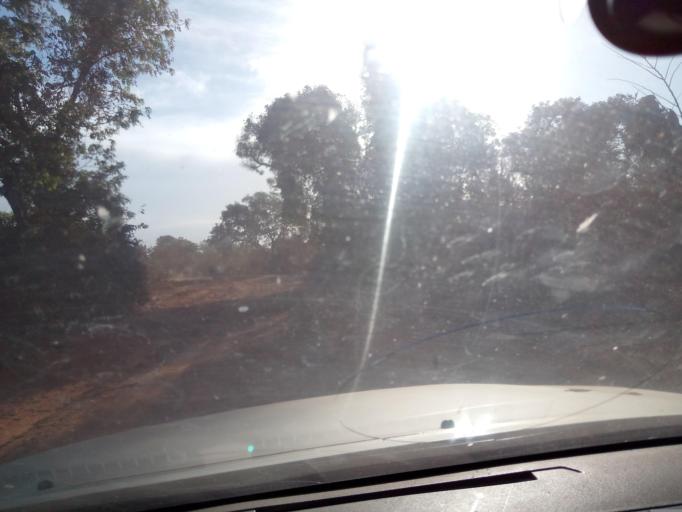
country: ML
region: Sikasso
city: Sikasso
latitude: 11.4360
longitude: -5.5568
